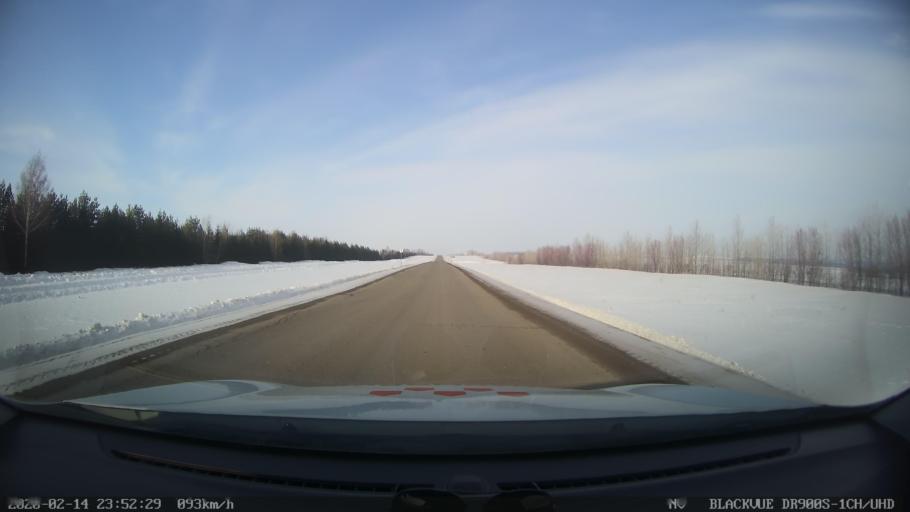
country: RU
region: Tatarstan
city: Kuybyshevskiy Zaton
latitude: 55.2793
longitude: 49.1435
